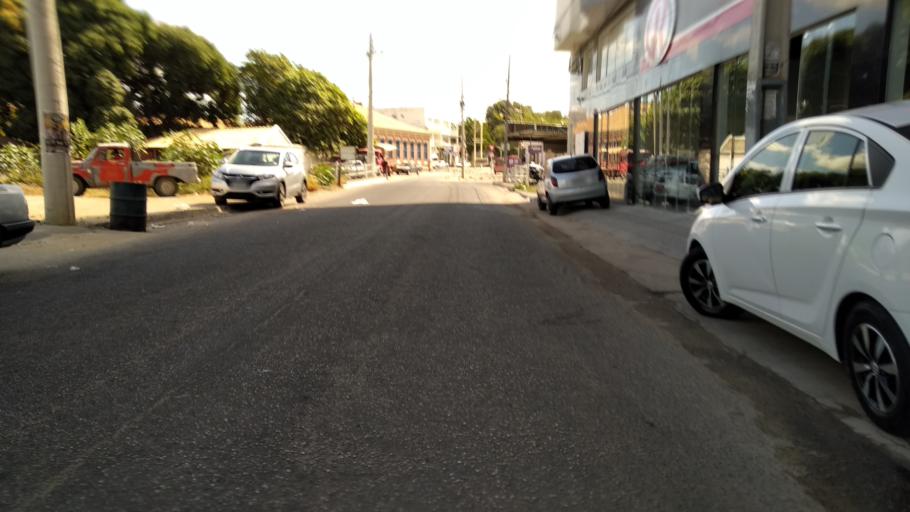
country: BR
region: Bahia
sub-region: Guanambi
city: Guanambi
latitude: -14.2312
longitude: -42.7805
